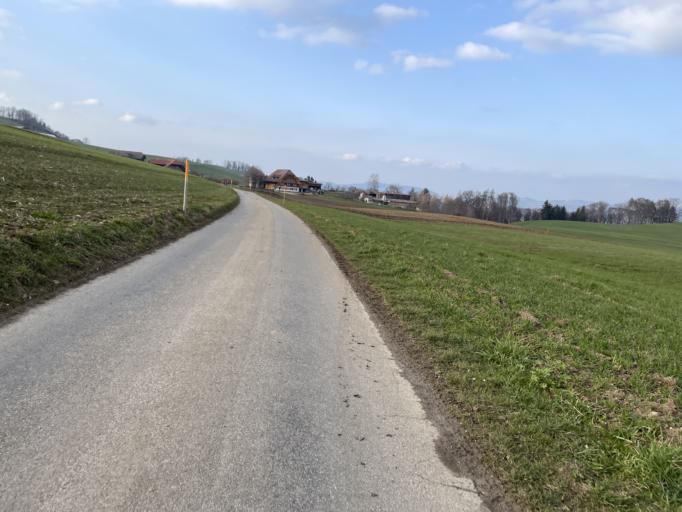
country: CH
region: Bern
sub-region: Bern-Mittelland District
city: Munsingen
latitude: 46.8685
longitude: 7.5280
